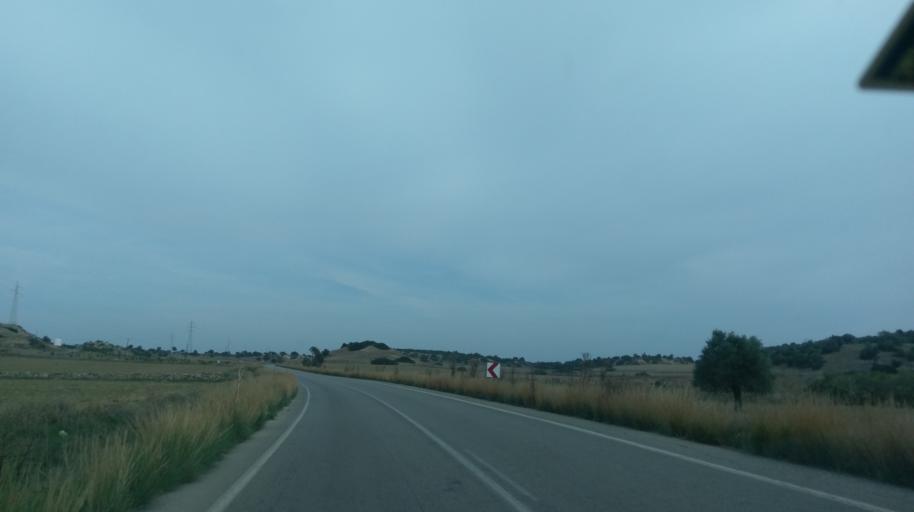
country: CY
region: Ammochostos
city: Leonarisso
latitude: 35.3857
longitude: 34.0498
